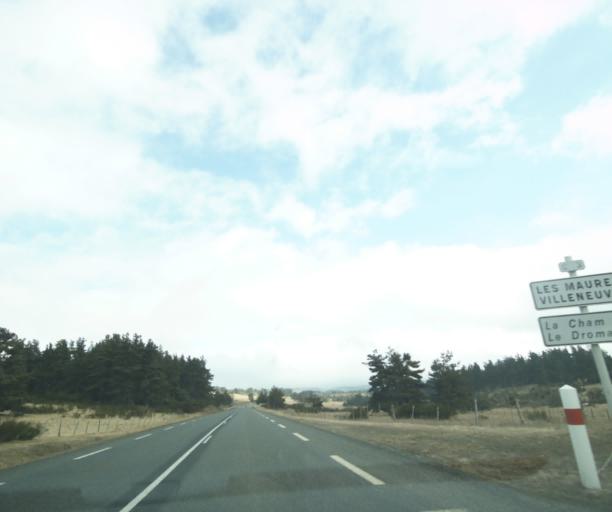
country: FR
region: Languedoc-Roussillon
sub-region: Departement de la Lozere
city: Langogne
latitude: 44.6400
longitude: 3.7024
